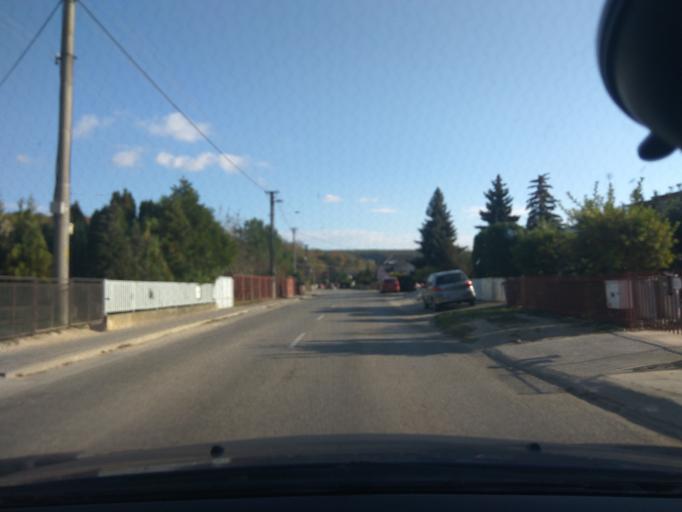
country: SK
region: Trnavsky
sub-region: Okres Trnava
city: Piestany
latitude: 48.5547
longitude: 17.8394
